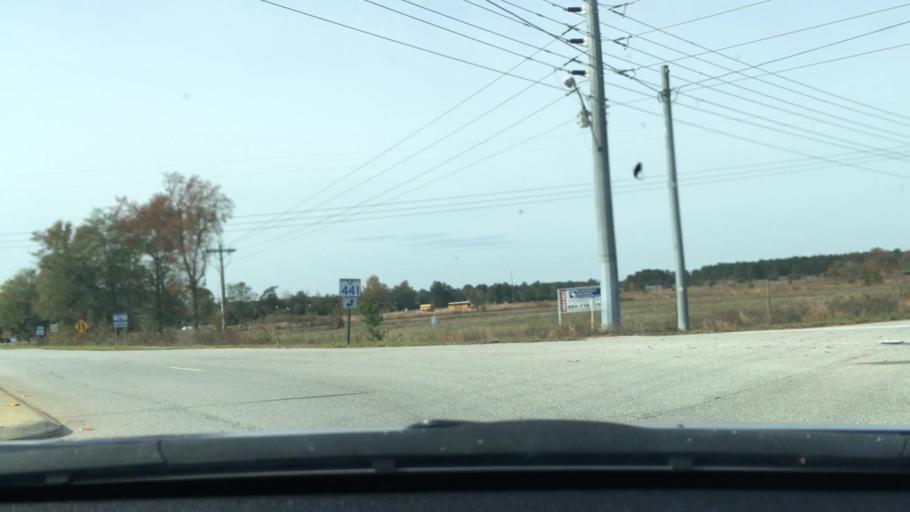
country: US
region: South Carolina
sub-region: Sumter County
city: Cherryvale
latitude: 33.9372
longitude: -80.4204
